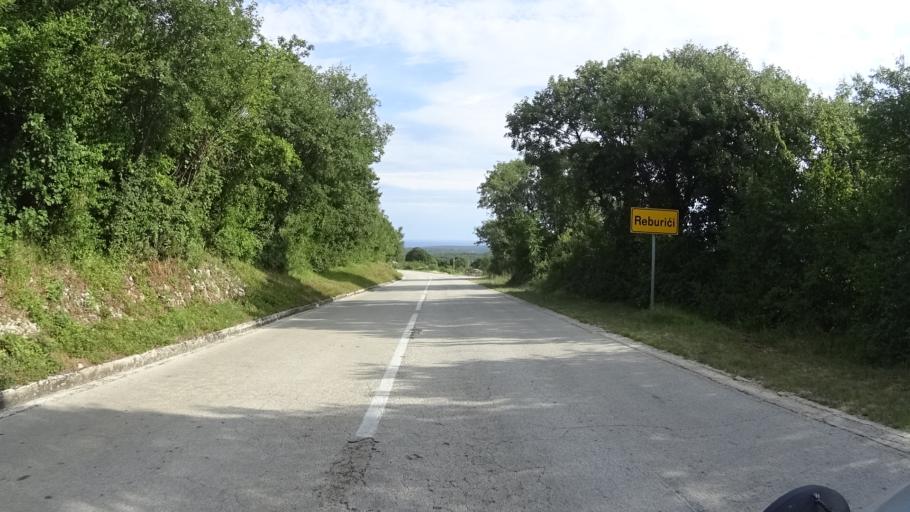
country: HR
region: Istarska
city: Rasa
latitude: 45.0381
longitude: 14.0791
